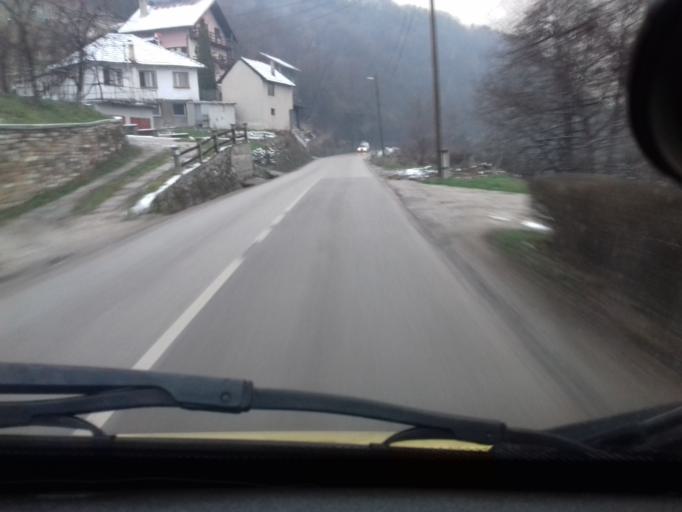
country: BA
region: Federation of Bosnia and Herzegovina
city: Zenica
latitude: 44.1873
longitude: 17.9426
